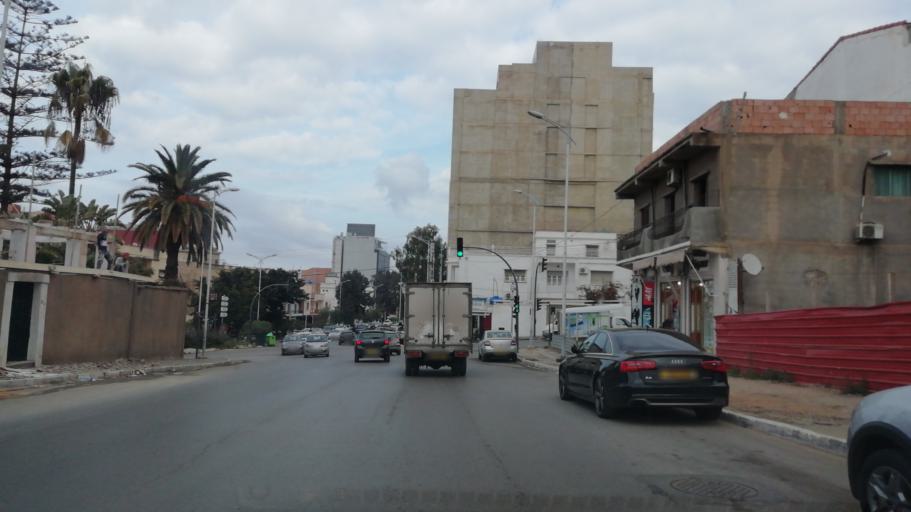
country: DZ
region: Oran
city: Oran
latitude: 35.7097
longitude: -0.6110
